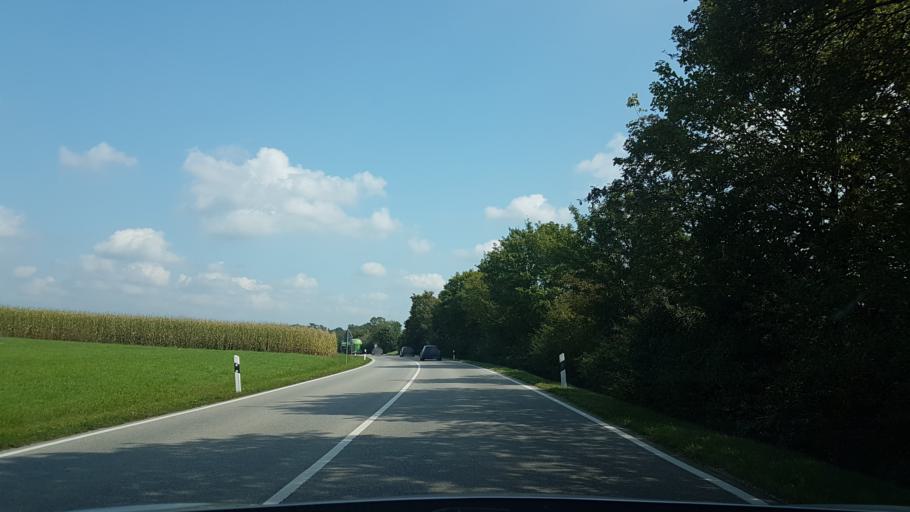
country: DE
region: Bavaria
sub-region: Upper Bavaria
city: Bockhorn
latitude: 48.3210
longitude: 11.9661
